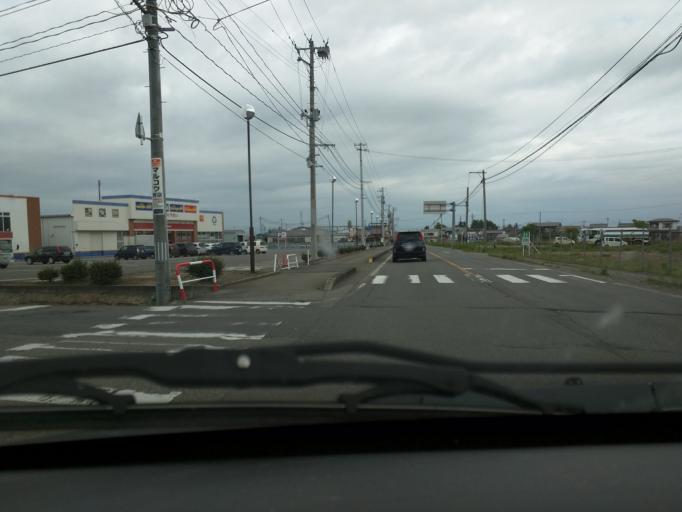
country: JP
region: Fukushima
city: Kitakata
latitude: 37.5190
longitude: 139.9256
